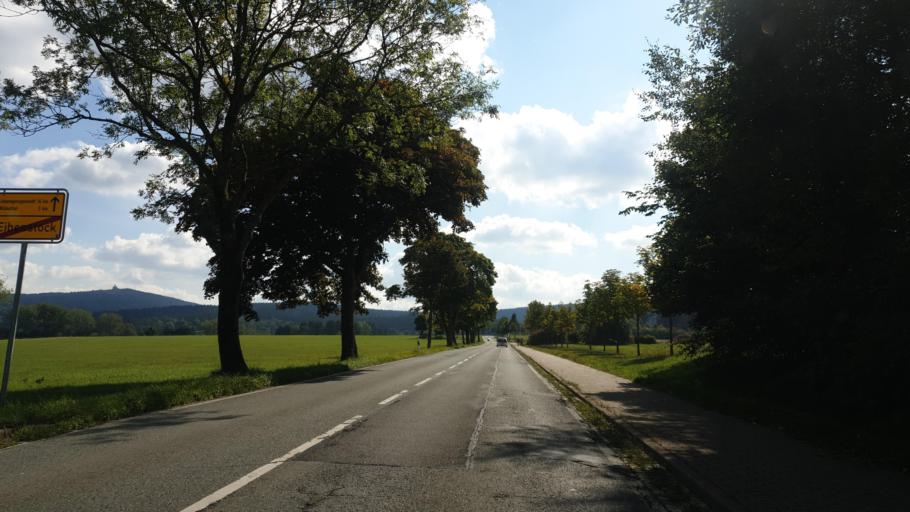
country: DE
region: Saxony
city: Eibenstock
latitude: 50.4879
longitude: 12.6081
